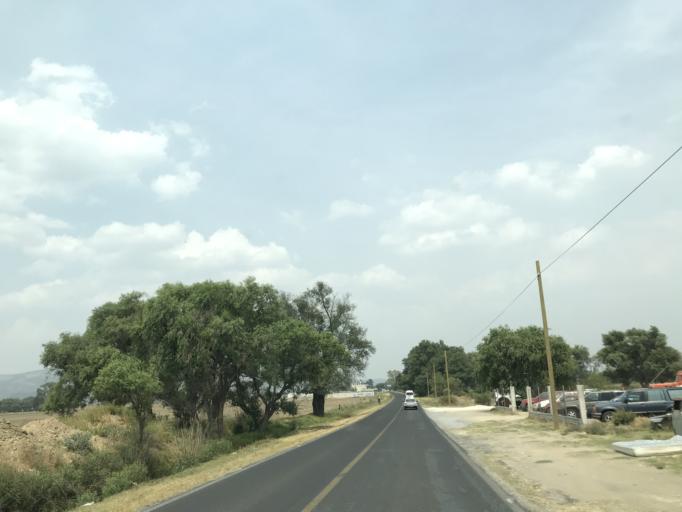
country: MX
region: Tlaxcala
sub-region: Ixtacuixtla de Mariano Matamoros
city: Santa Justina Ecatepec
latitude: 19.3140
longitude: -98.3331
